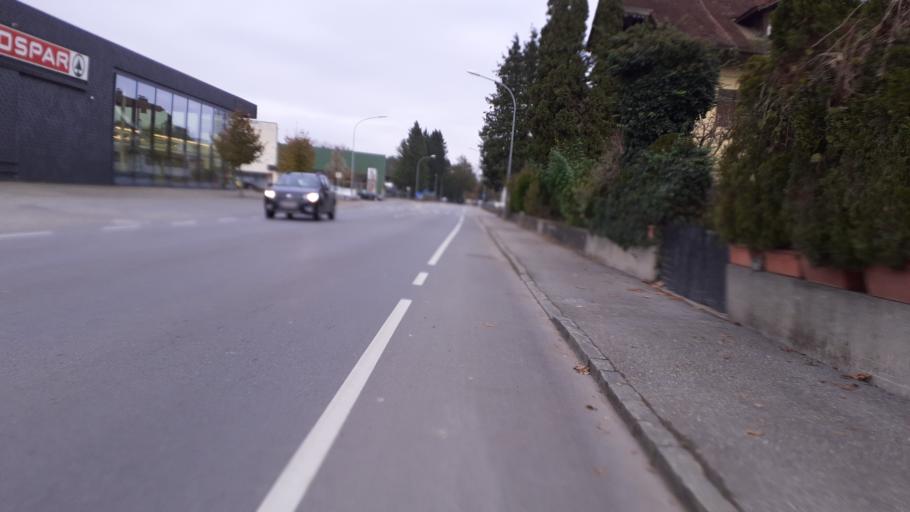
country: AT
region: Vorarlberg
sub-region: Politischer Bezirk Feldkirch
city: Nofels
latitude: 47.2480
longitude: 9.5885
